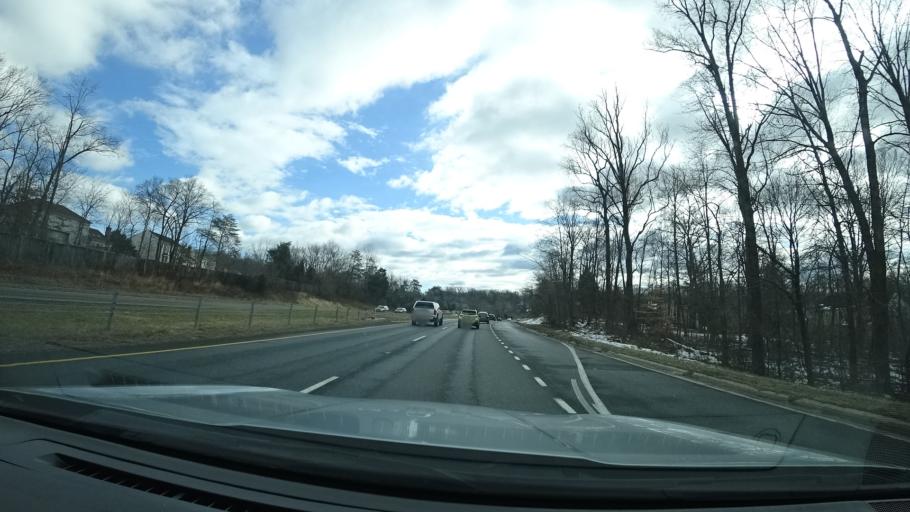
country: US
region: Virginia
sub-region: Fairfax County
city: Dranesville
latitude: 38.9902
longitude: -77.3625
